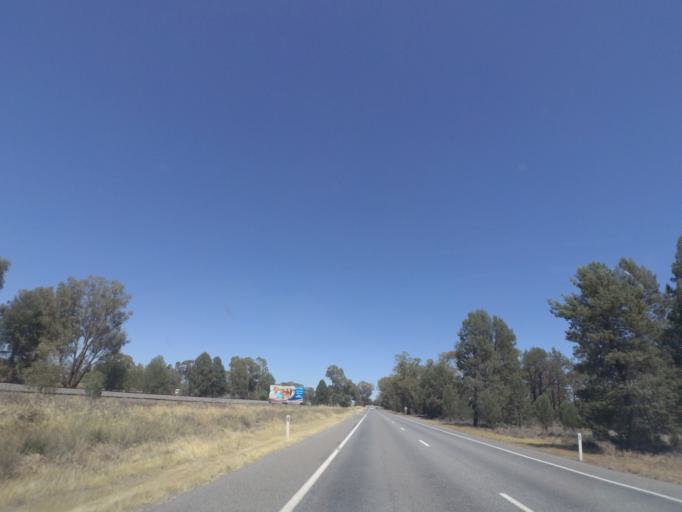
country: AU
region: New South Wales
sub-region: Narrandera
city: Narrandera
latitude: -34.7375
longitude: 146.5859
